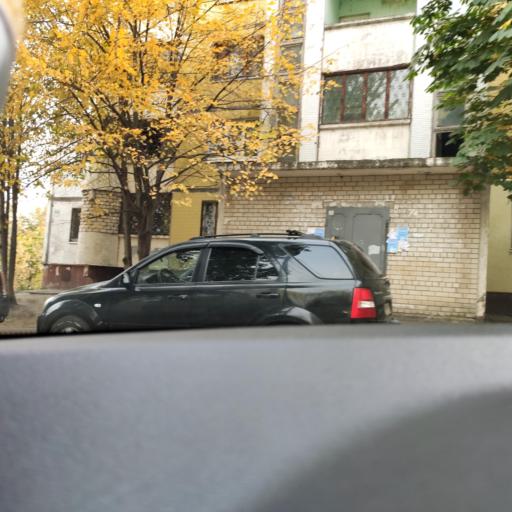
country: RU
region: Samara
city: Samara
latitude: 53.2071
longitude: 50.2148
